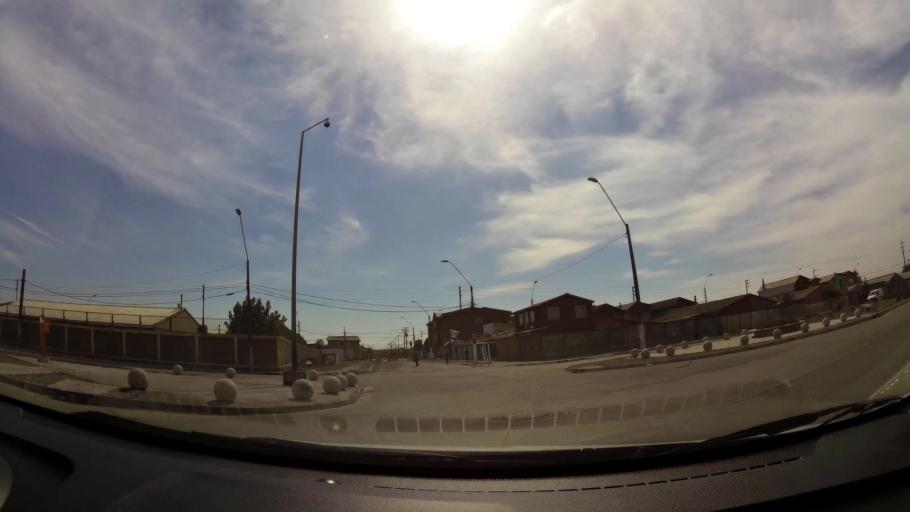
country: CL
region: Biobio
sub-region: Provincia de Concepcion
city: Talcahuano
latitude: -36.7344
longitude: -73.1130
